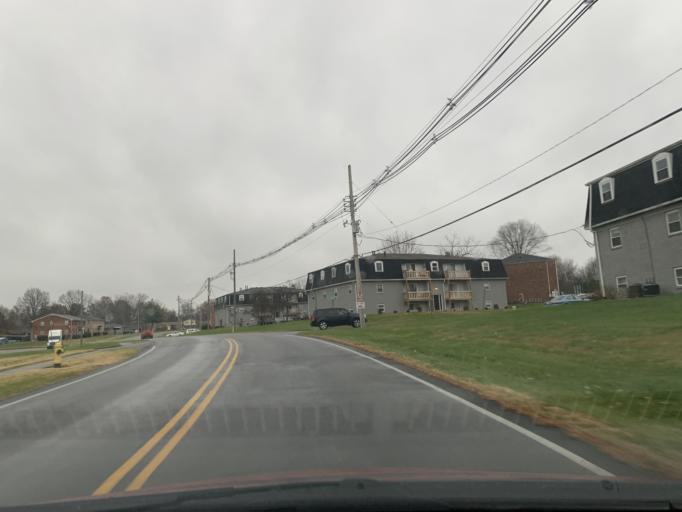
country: US
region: Kentucky
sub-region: Jefferson County
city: Saint Regis Park
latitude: 38.1981
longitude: -85.6222
